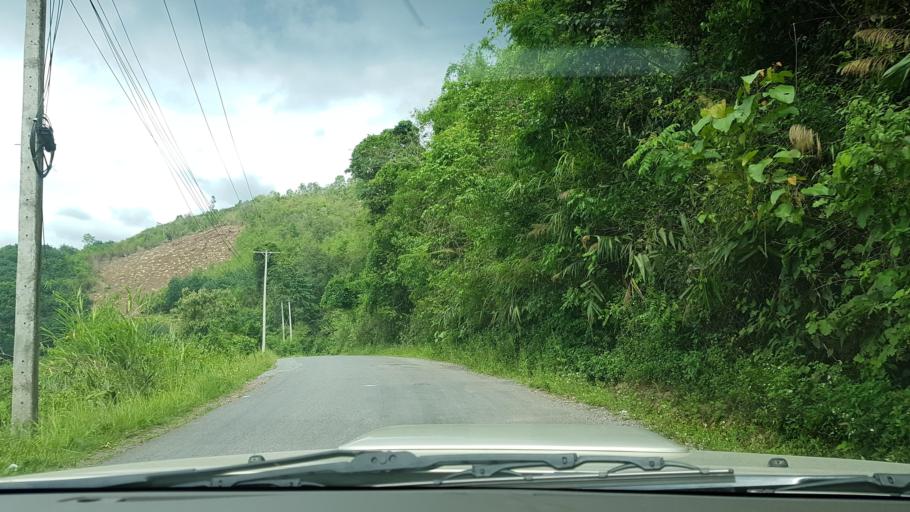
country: LA
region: Loungnamtha
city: Muang Nale
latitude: 20.3677
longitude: 101.7169
